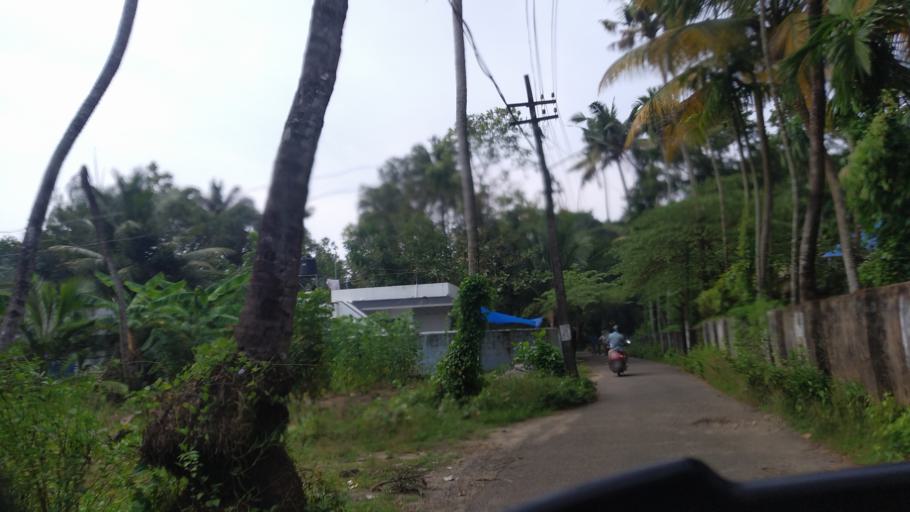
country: IN
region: Kerala
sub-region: Ernakulam
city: Elur
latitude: 10.0535
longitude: 76.2205
